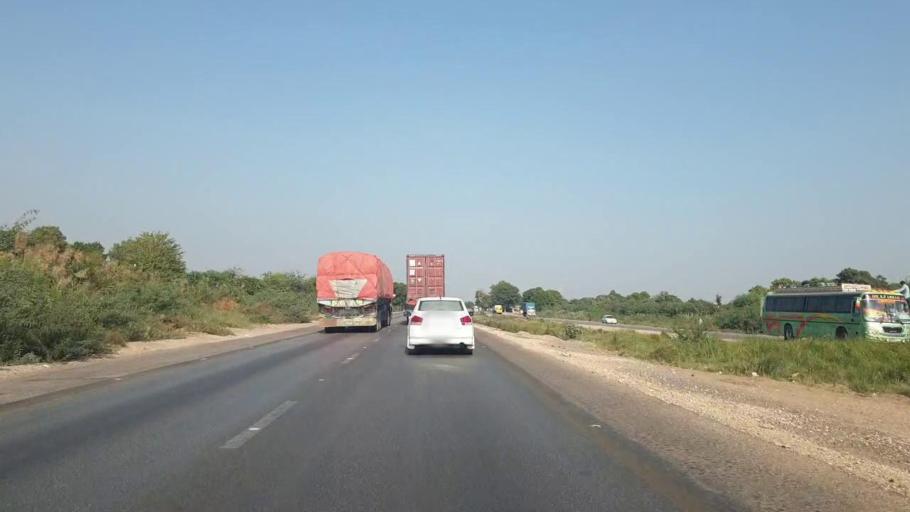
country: PK
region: Sindh
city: Hyderabad
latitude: 25.4865
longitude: 68.4181
